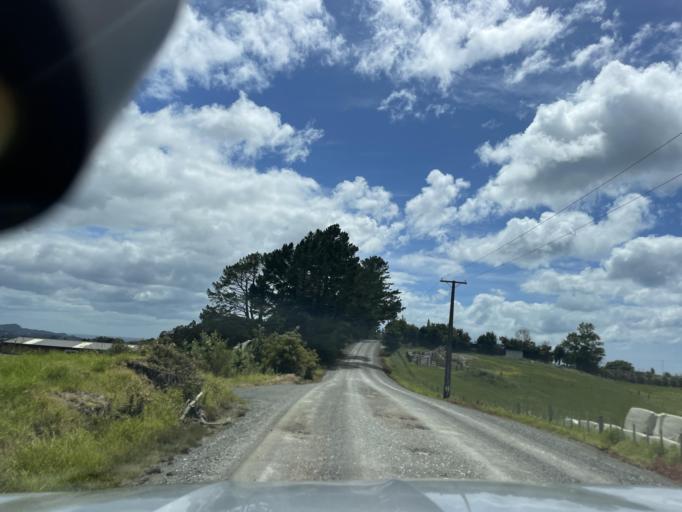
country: NZ
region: Auckland
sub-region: Auckland
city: Wellsford
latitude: -36.1718
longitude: 174.5784
